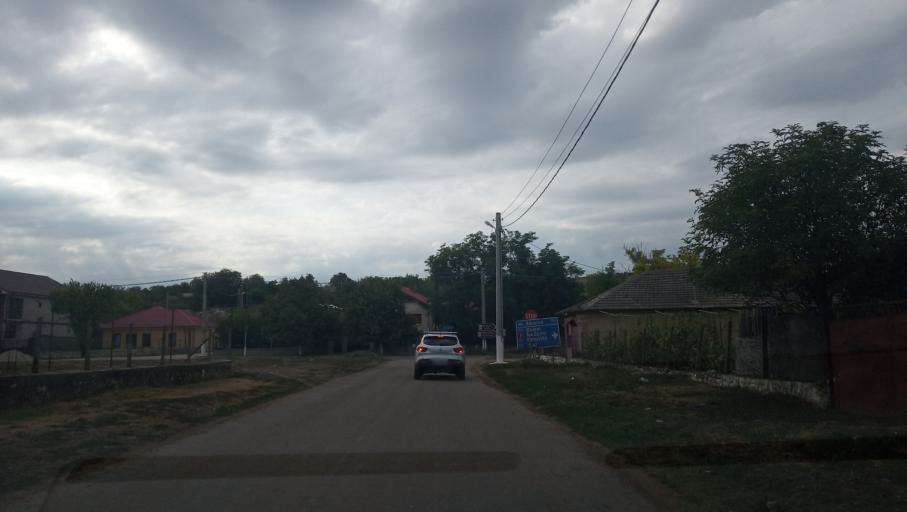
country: RO
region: Constanta
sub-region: Comuna Adamclisi
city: Adamclisi
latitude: 44.0444
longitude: 27.9591
